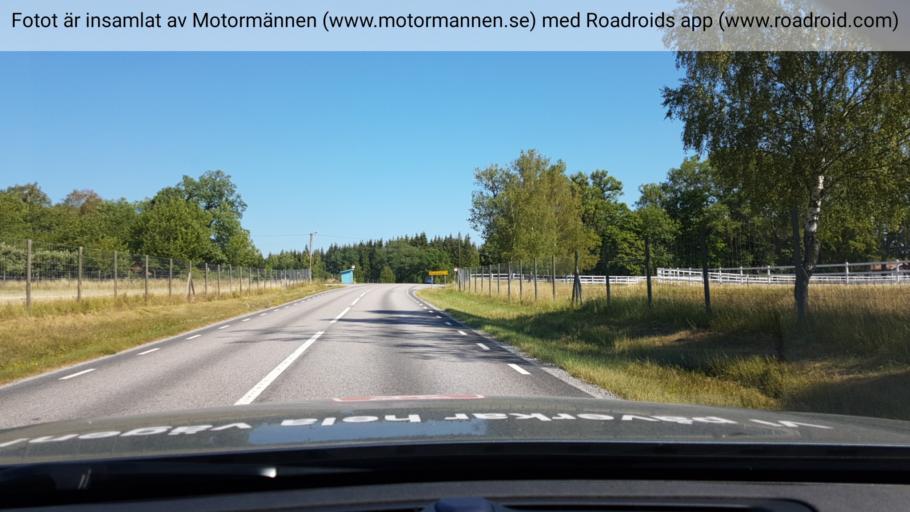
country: SE
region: Stockholm
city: Stenhamra
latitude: 59.3250
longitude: 17.6329
